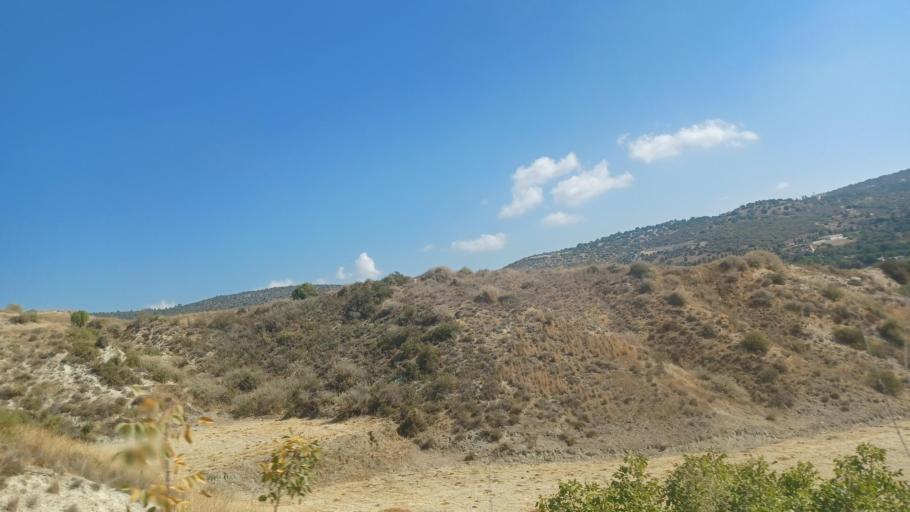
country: CY
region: Pafos
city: Polis
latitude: 34.9894
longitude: 32.4685
